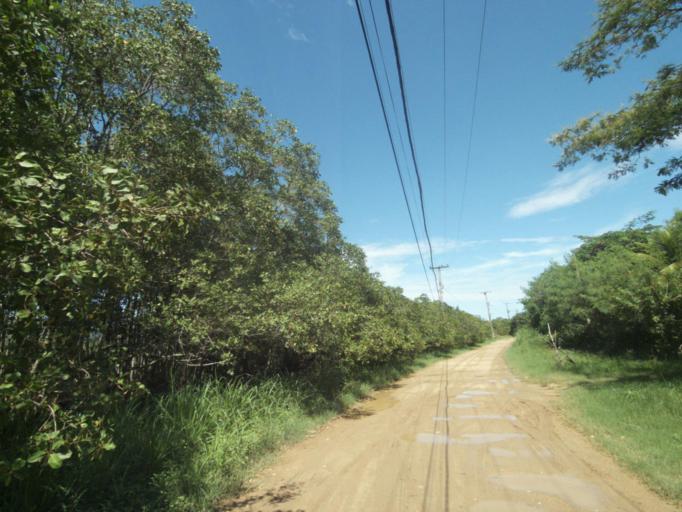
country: BR
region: Rio de Janeiro
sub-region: Niteroi
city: Niteroi
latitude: -22.9506
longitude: -43.0452
